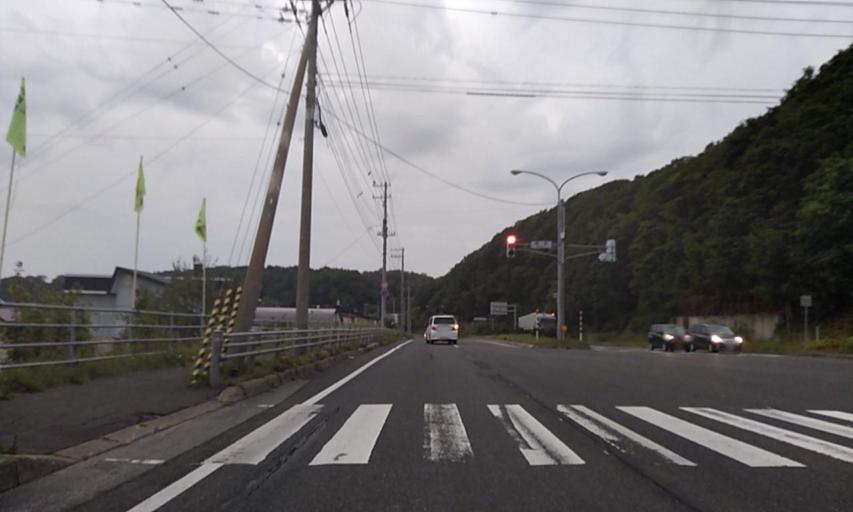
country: JP
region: Hokkaido
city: Abashiri
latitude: 43.9906
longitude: 144.2969
